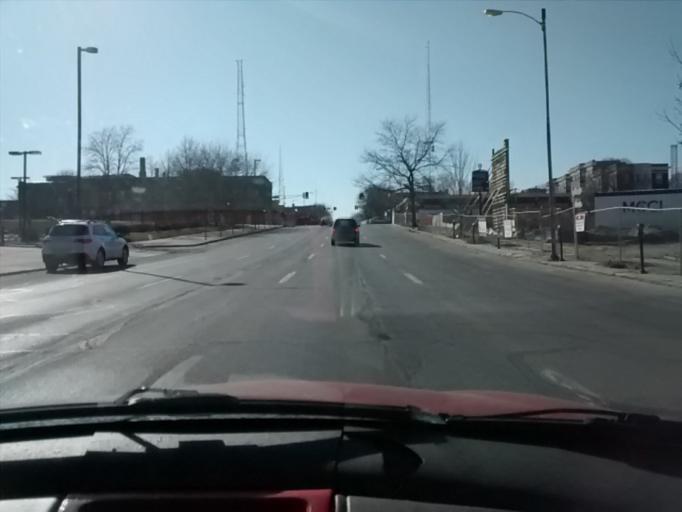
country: US
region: Nebraska
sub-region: Douglas County
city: Omaha
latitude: 41.2577
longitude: -95.9452
